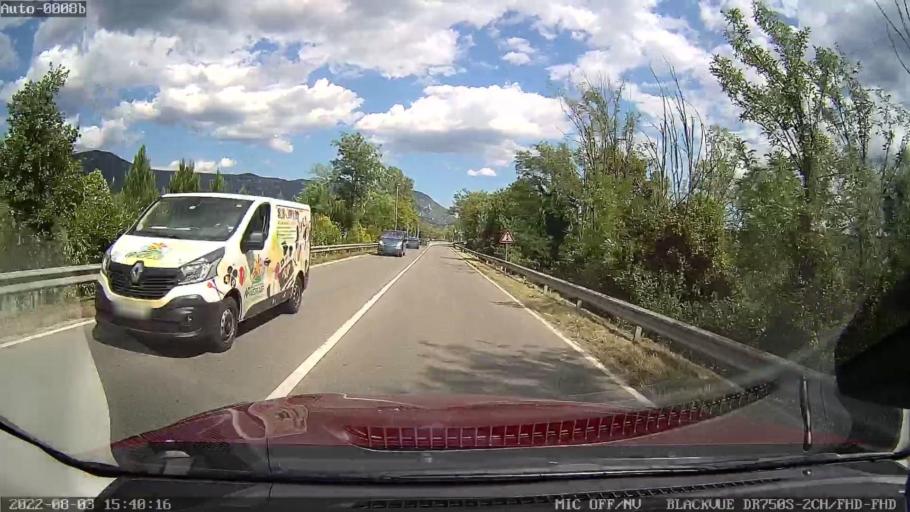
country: SI
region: Nova Gorica
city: Kromberk
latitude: 45.9568
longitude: 13.6685
